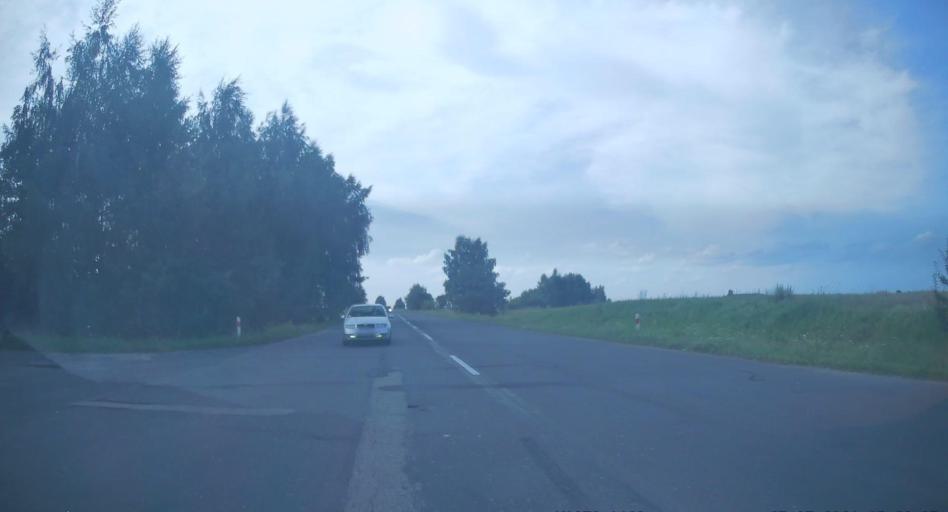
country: PL
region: Lodz Voivodeship
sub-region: Powiat tomaszowski
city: Rzeczyca
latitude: 51.6484
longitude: 20.2814
